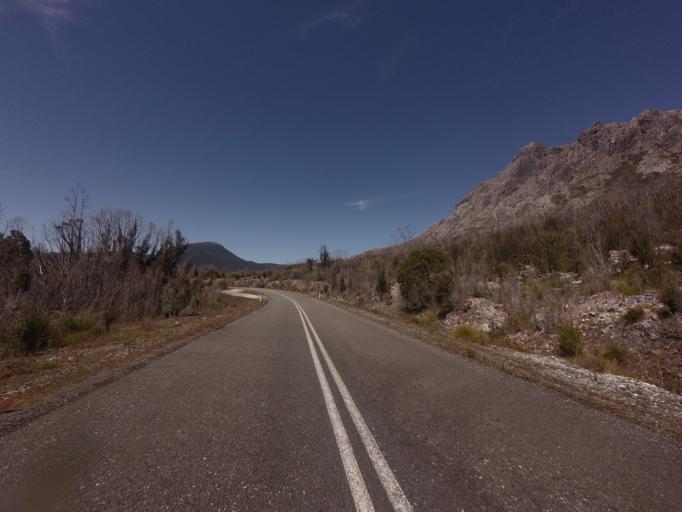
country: AU
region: Tasmania
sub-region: Huon Valley
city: Geeveston
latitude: -42.8604
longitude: 146.2269
